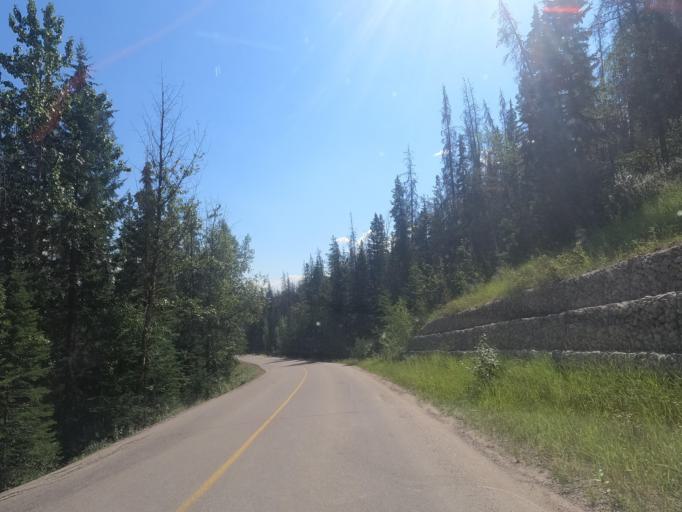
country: CA
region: Alberta
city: Jasper Park Lodge
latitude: 52.8570
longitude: -118.0957
